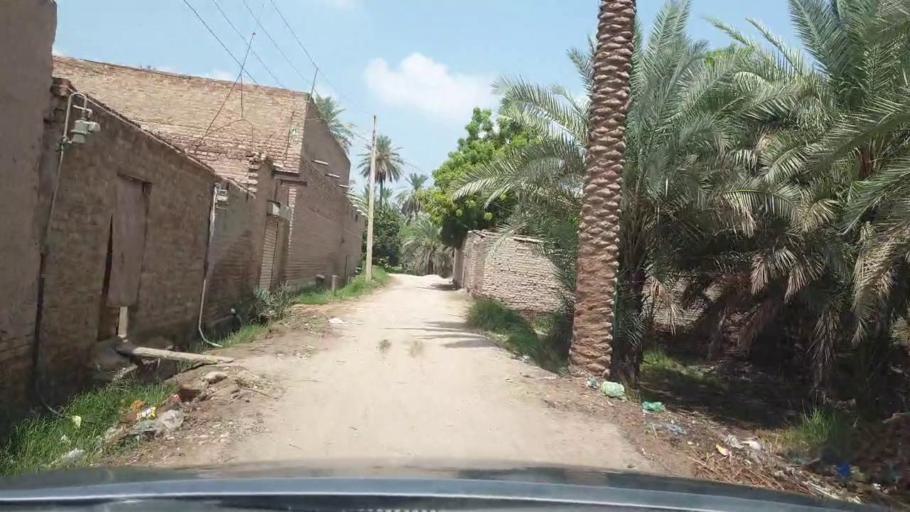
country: PK
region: Sindh
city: Pir jo Goth
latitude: 27.6102
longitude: 68.6655
